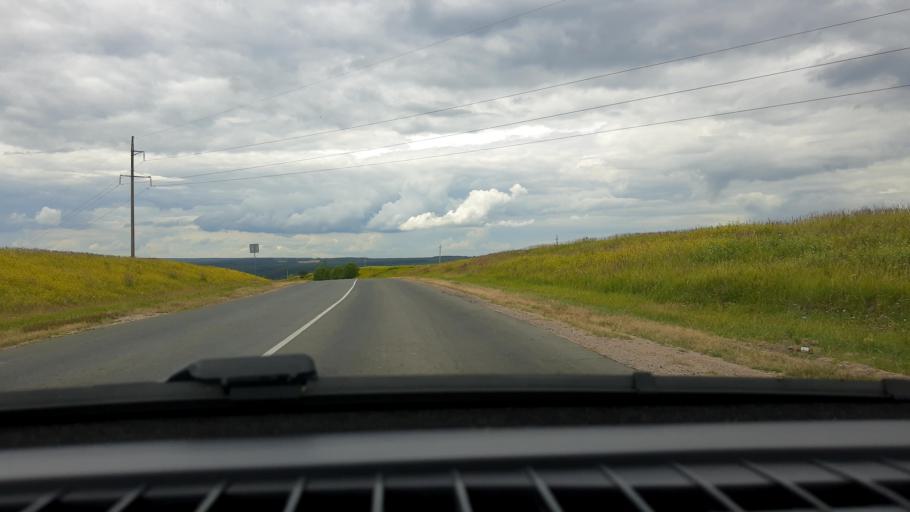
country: RU
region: Nizjnij Novgorod
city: Sergach
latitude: 55.5750
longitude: 45.4187
